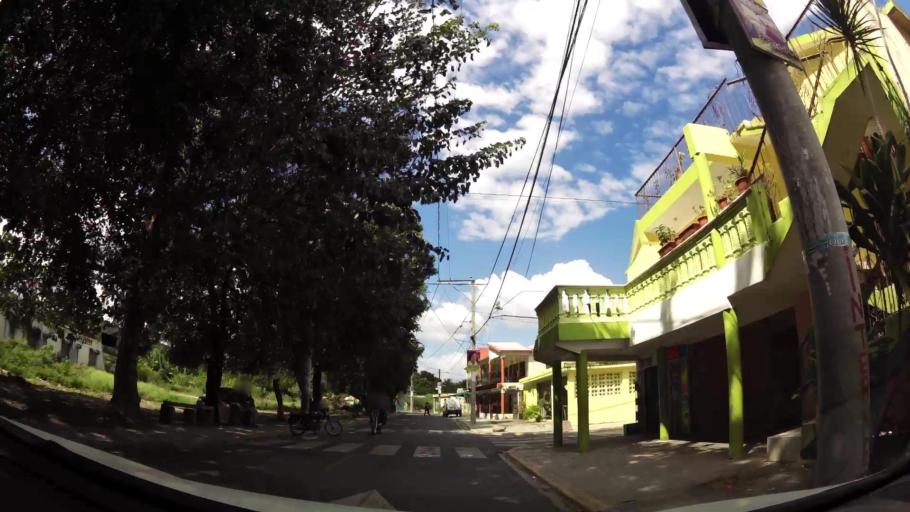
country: DO
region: San Cristobal
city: San Cristobal
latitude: 18.4214
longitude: -70.0945
